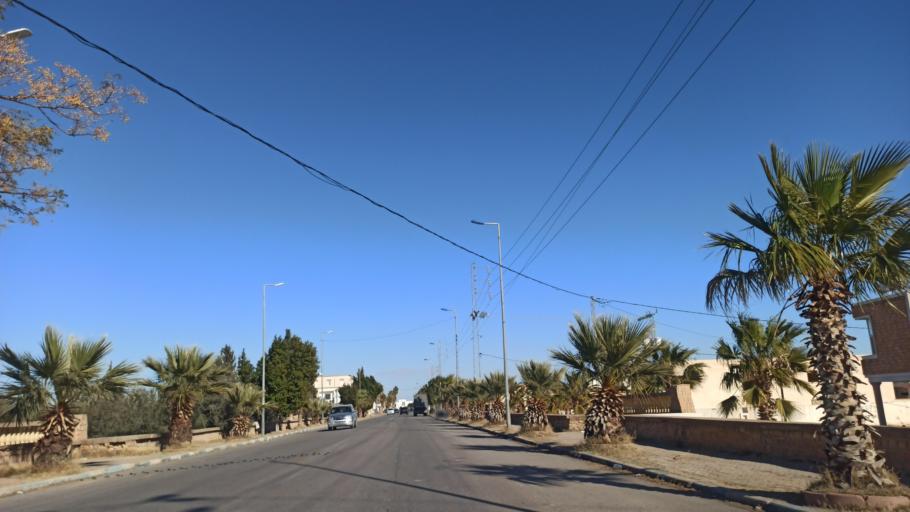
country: TN
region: Sidi Bu Zayd
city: Jilma
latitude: 35.2666
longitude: 9.4140
